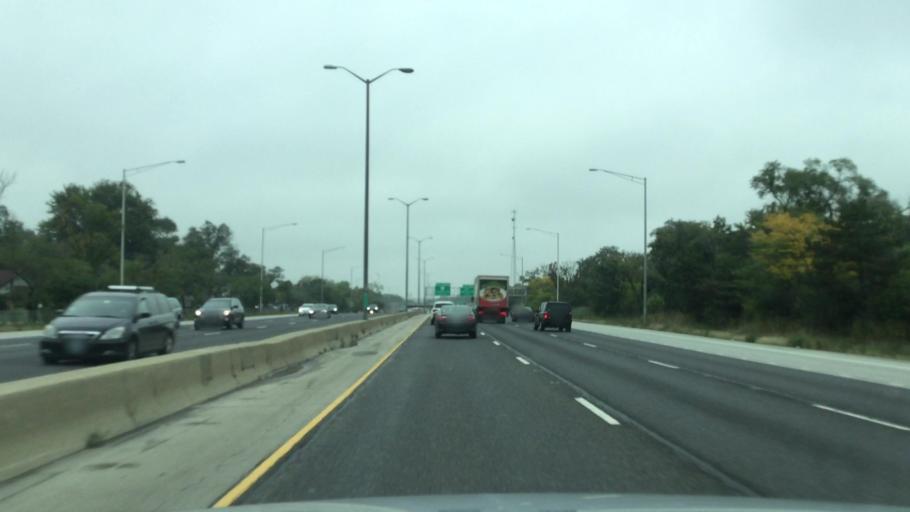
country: US
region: Illinois
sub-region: Cook County
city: Northfield
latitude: 42.0980
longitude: -87.7654
